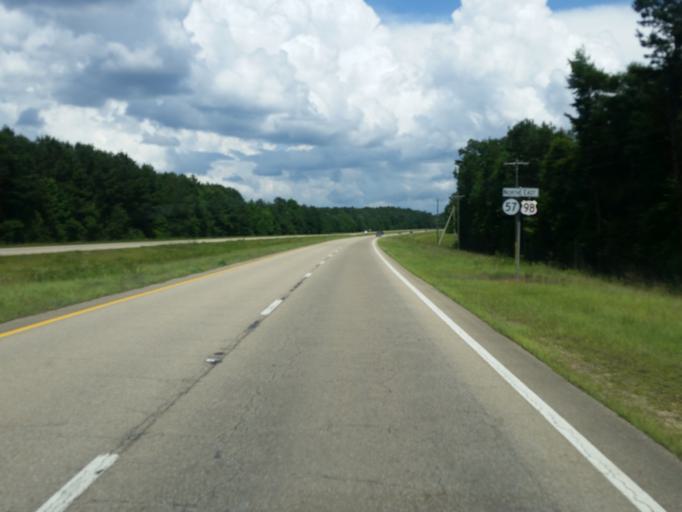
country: US
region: Mississippi
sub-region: Greene County
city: Leakesville
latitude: 31.1077
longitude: -88.7987
